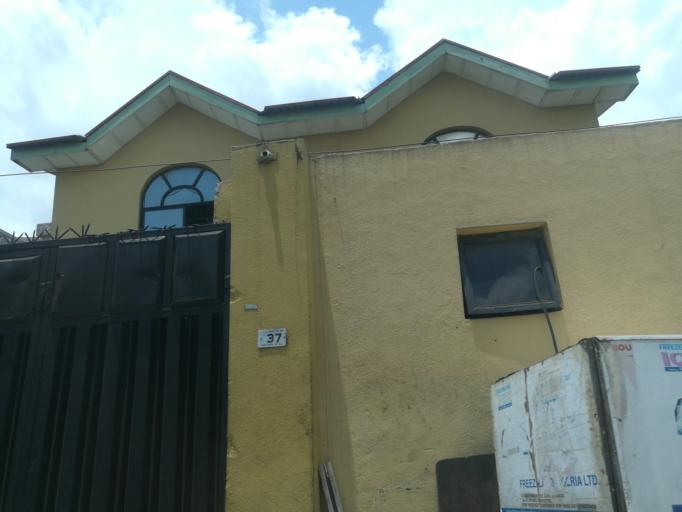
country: NG
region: Lagos
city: Somolu
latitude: 6.5494
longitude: 3.3606
